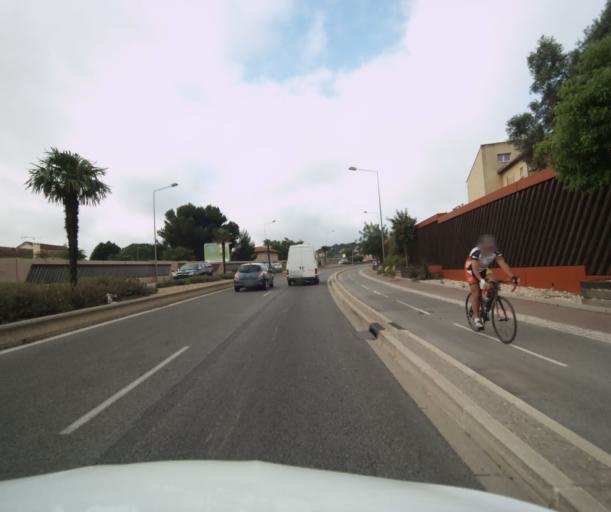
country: FR
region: Provence-Alpes-Cote d'Azur
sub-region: Departement du Var
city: Six-Fours-les-Plages
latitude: 43.1028
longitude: 5.8540
